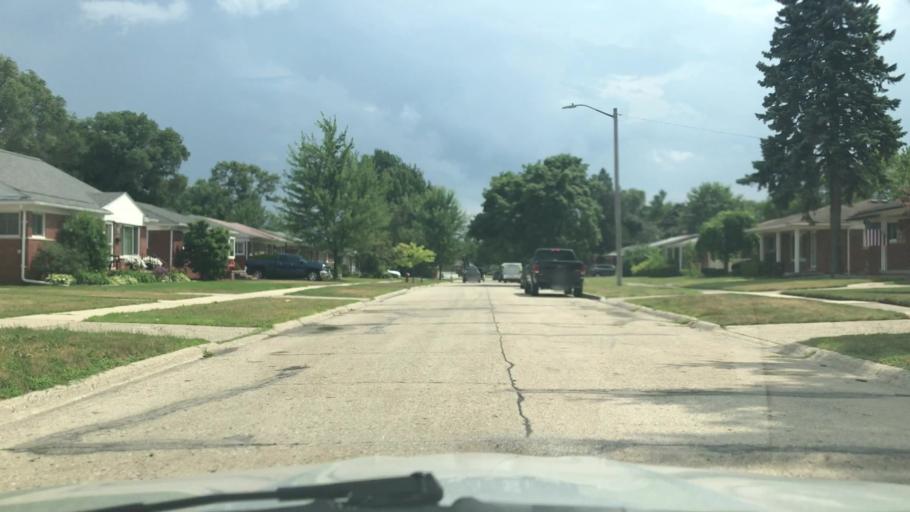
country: US
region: Michigan
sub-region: Oakland County
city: Madison Heights
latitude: 42.5075
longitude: -83.1222
